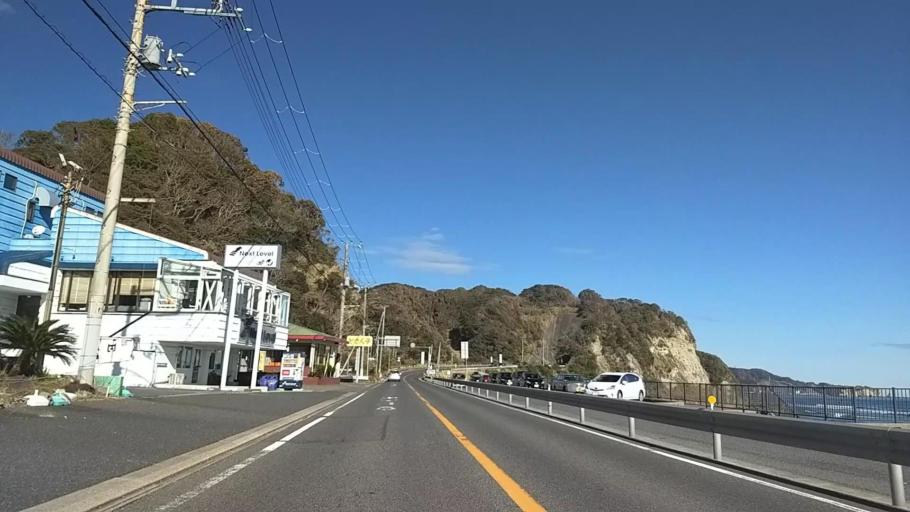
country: JP
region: Chiba
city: Katsuura
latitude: 35.1693
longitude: 140.3376
